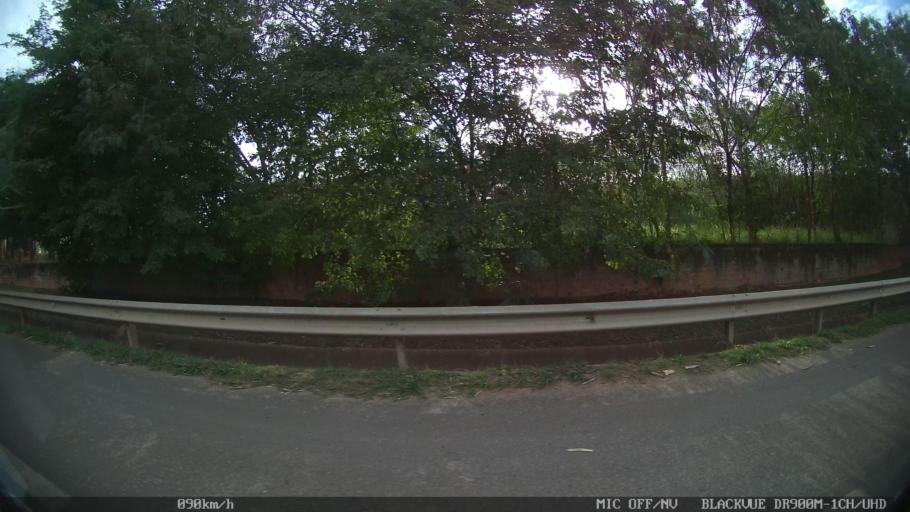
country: BR
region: Sao Paulo
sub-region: Cosmopolis
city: Cosmopolis
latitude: -22.6244
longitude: -47.2017
